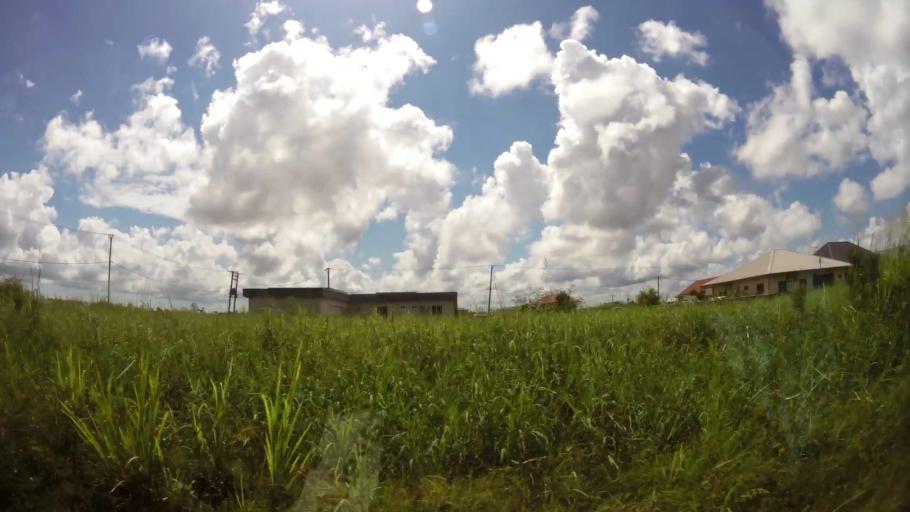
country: SR
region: Paramaribo
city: Paramaribo
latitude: 5.8712
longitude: -55.1333
